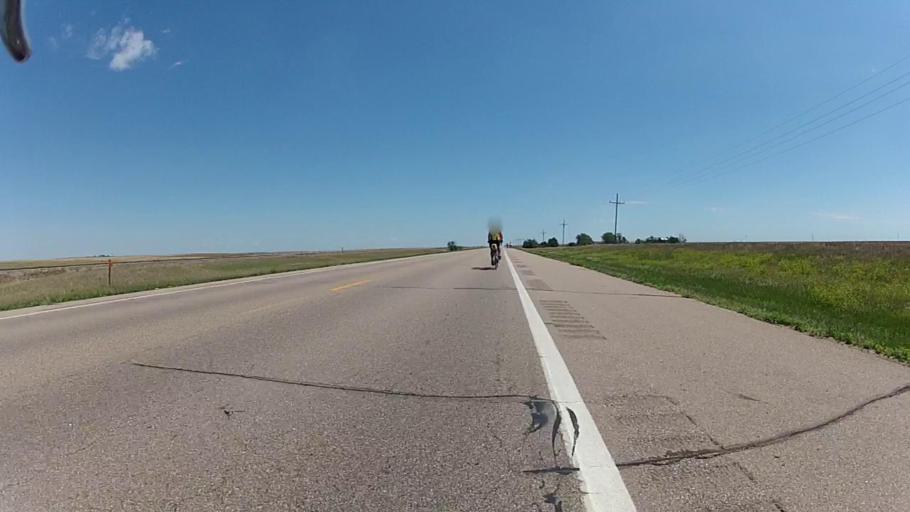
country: US
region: Kansas
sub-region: Ford County
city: Dodge City
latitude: 37.6730
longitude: -100.1928
